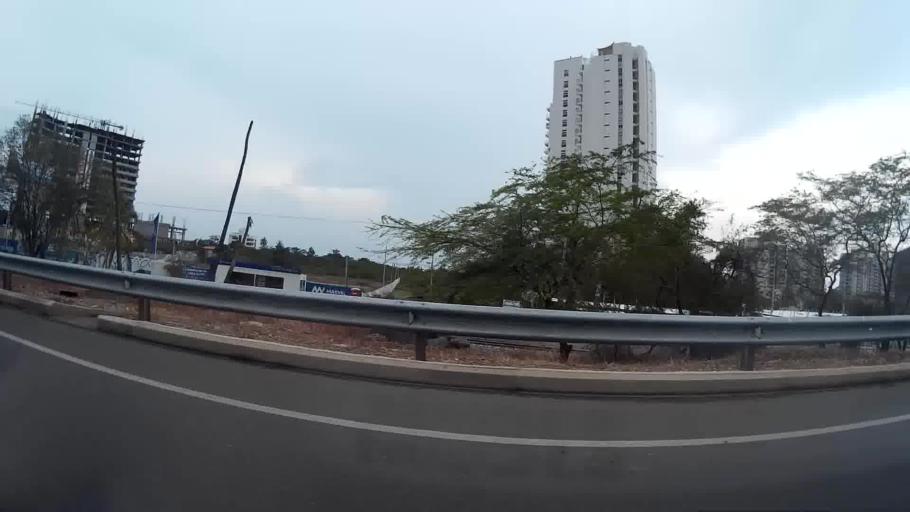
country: CO
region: Magdalena
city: Santa Marta
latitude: 11.1717
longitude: -74.2308
